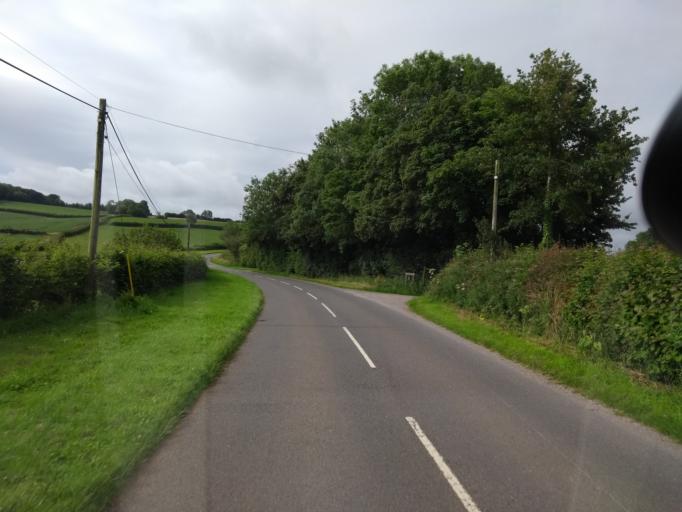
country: GB
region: England
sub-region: Somerset
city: Wiveliscombe
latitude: 51.0619
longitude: -3.2877
